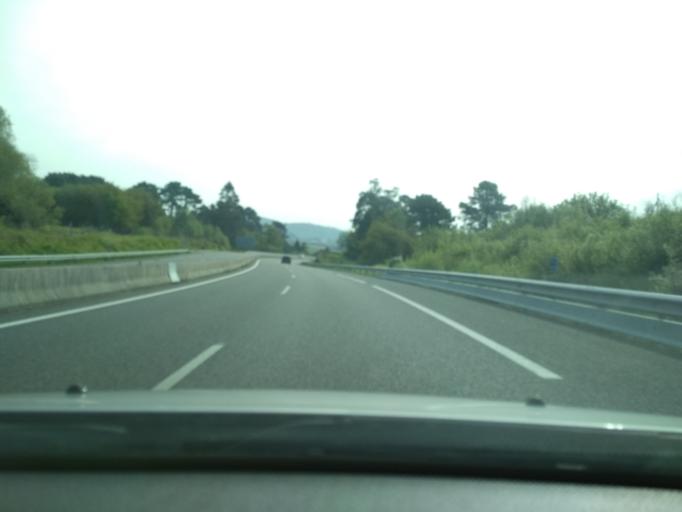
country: ES
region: Galicia
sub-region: Provincia da Coruna
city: Rianxo
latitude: 42.6689
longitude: -8.8232
